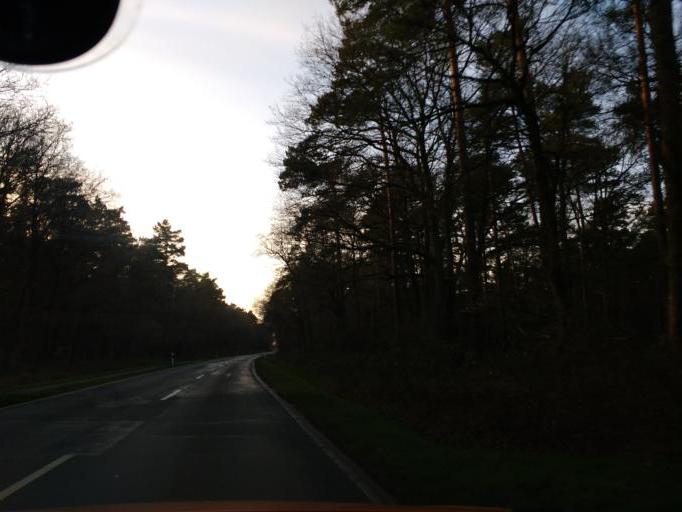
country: DE
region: Lower Saxony
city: Hude
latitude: 53.0954
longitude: 8.4138
